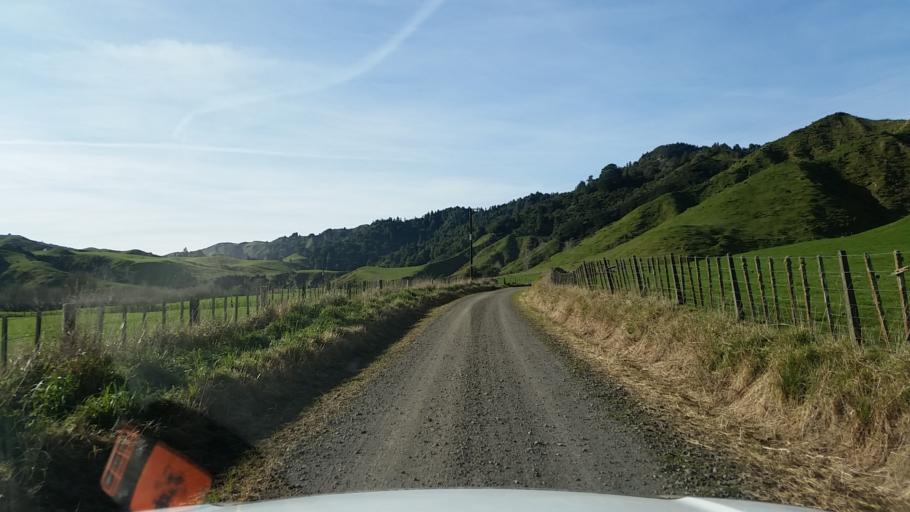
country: NZ
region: Taranaki
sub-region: South Taranaki District
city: Eltham
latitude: -39.3106
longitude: 174.5451
